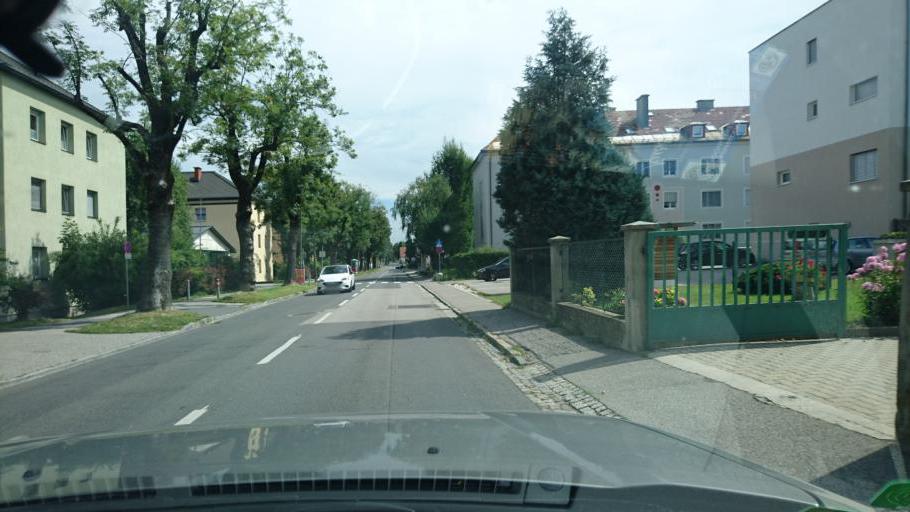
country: AT
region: Carinthia
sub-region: Villach Stadt
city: Villach
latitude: 46.6149
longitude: 13.8602
